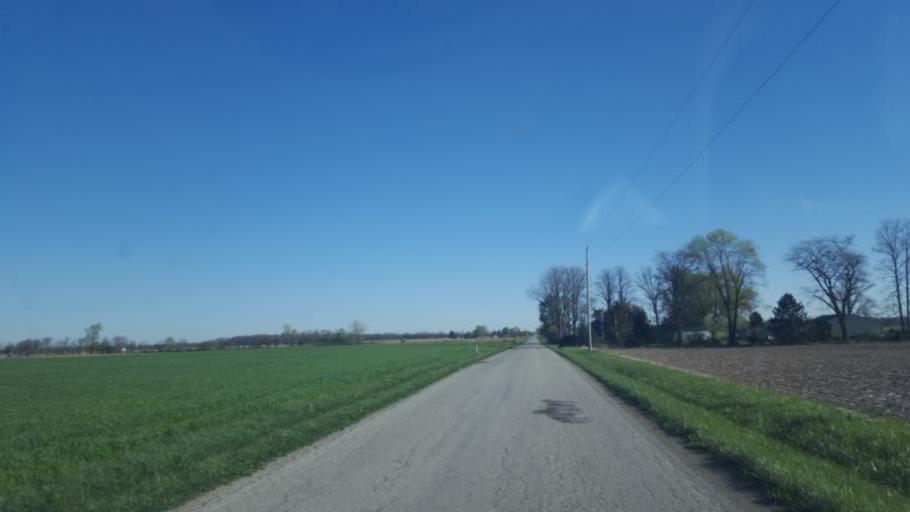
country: US
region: Ohio
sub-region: Morrow County
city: Mount Gilead
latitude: 40.6069
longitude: -82.9185
